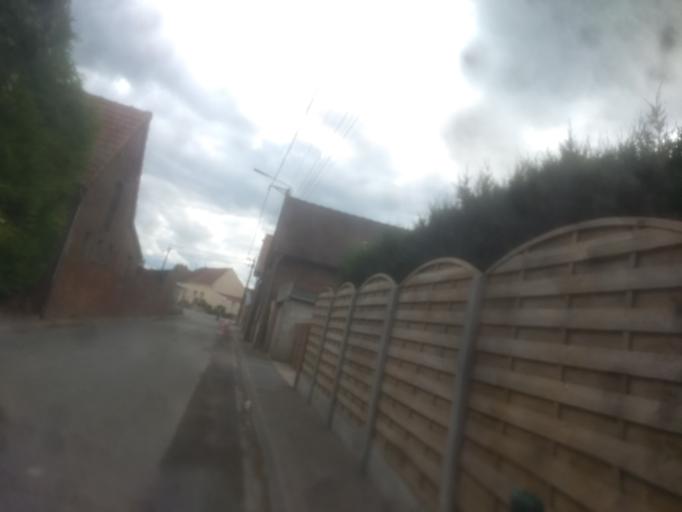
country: FR
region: Nord-Pas-de-Calais
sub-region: Departement du Pas-de-Calais
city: Agny
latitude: 50.2281
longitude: 2.7383
